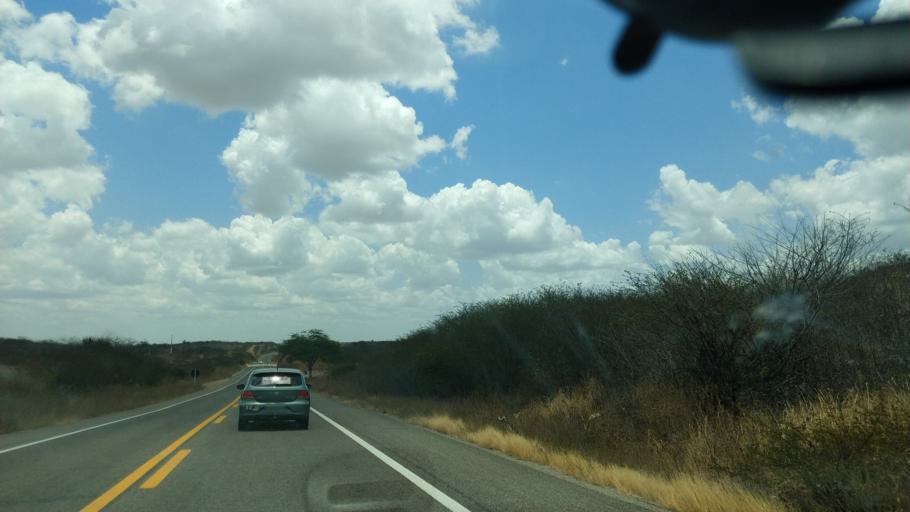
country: BR
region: Rio Grande do Norte
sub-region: Cerro Cora
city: Cerro Cora
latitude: -6.2095
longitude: -36.2942
